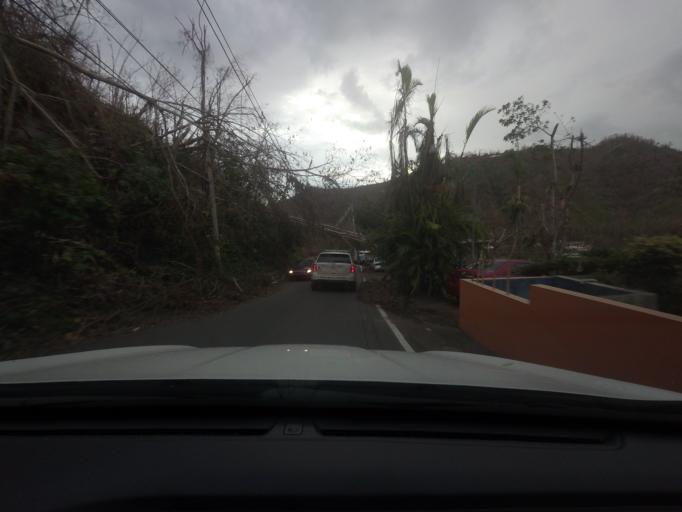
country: PR
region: Ciales
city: Ciales
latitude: 18.2901
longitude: -66.4848
